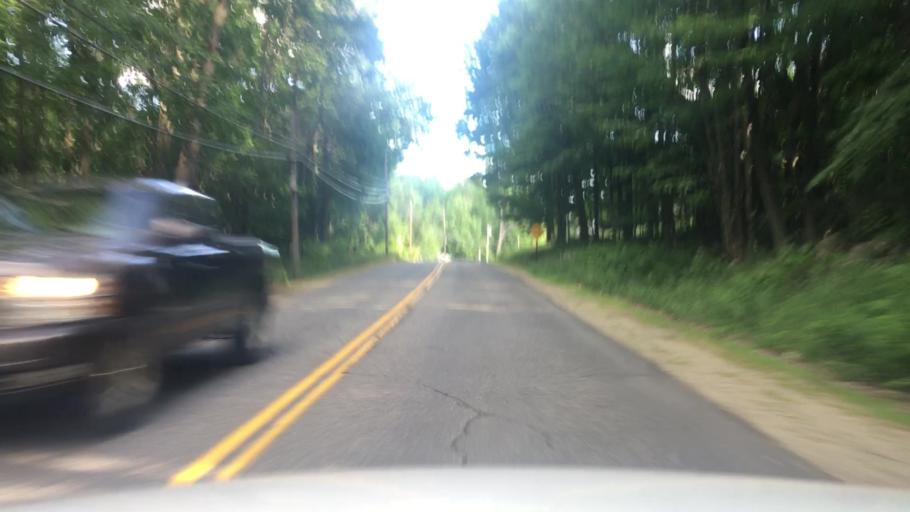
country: US
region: Maine
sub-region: Franklin County
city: Wilton
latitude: 44.5798
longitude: -70.2331
